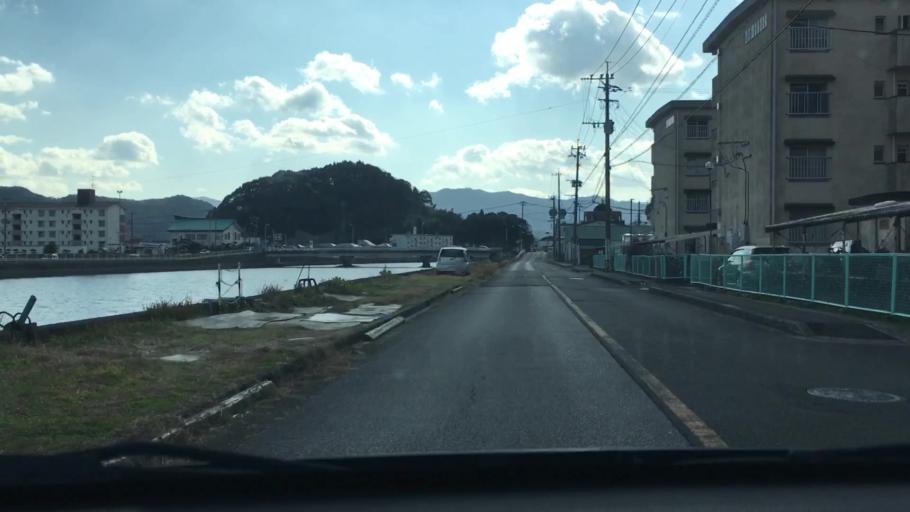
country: JP
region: Oita
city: Saiki
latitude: 32.9639
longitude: 131.9128
